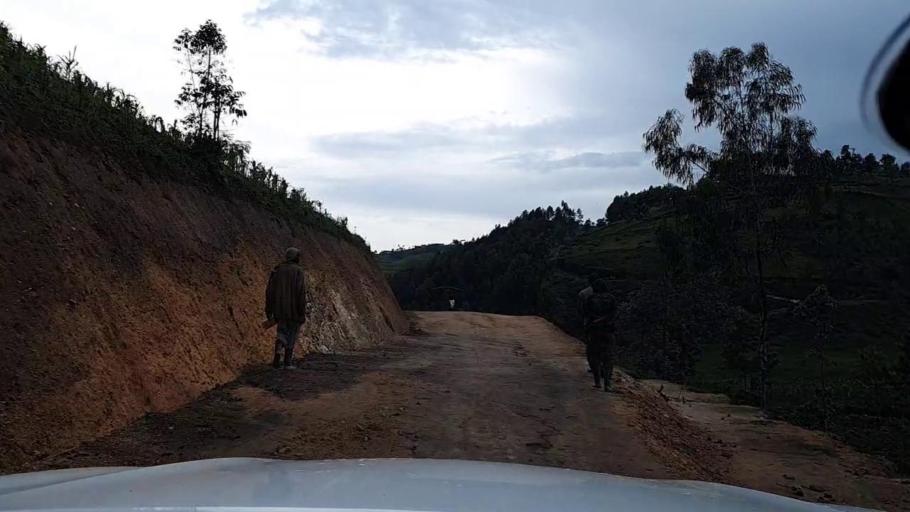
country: BI
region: Kayanza
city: Kayanza
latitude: -2.7726
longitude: 29.4461
